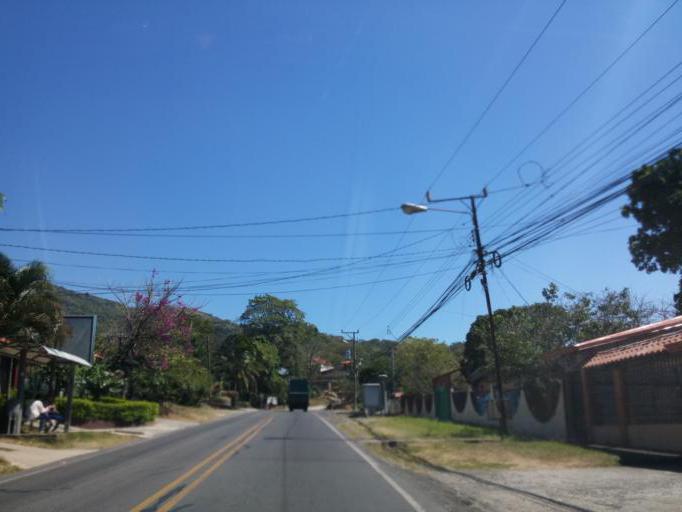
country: CR
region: Heredia
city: Colon
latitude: 9.9093
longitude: -84.2383
